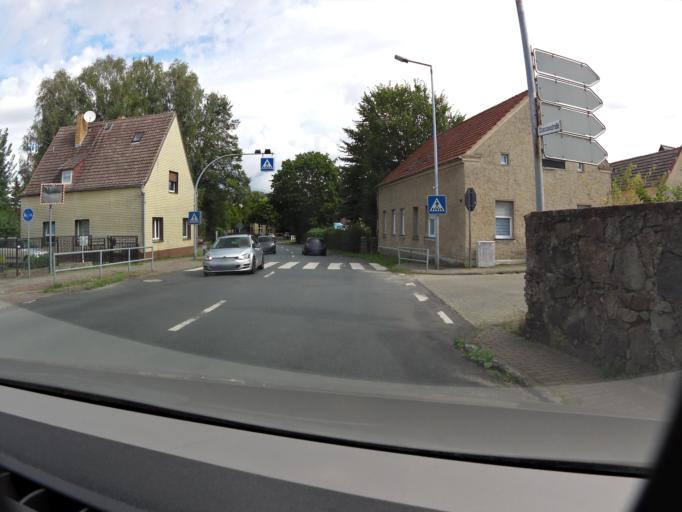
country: DE
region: Brandenburg
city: Rauen
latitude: 52.3283
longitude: 14.0257
